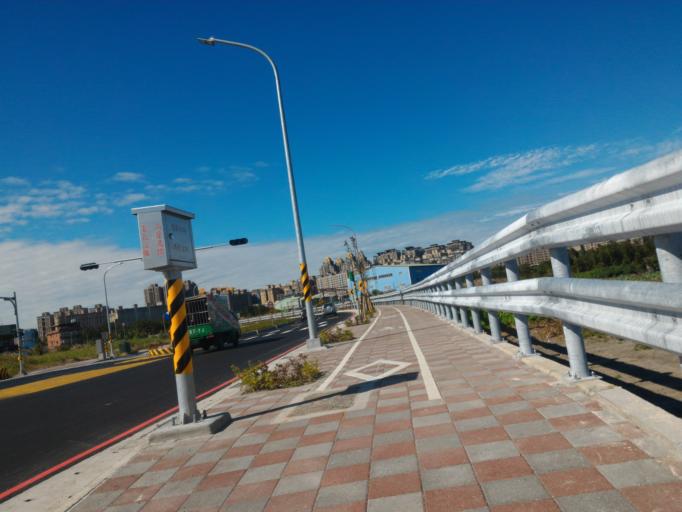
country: TW
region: Taiwan
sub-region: Taoyuan
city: Taoyuan
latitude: 24.9390
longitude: 121.3873
